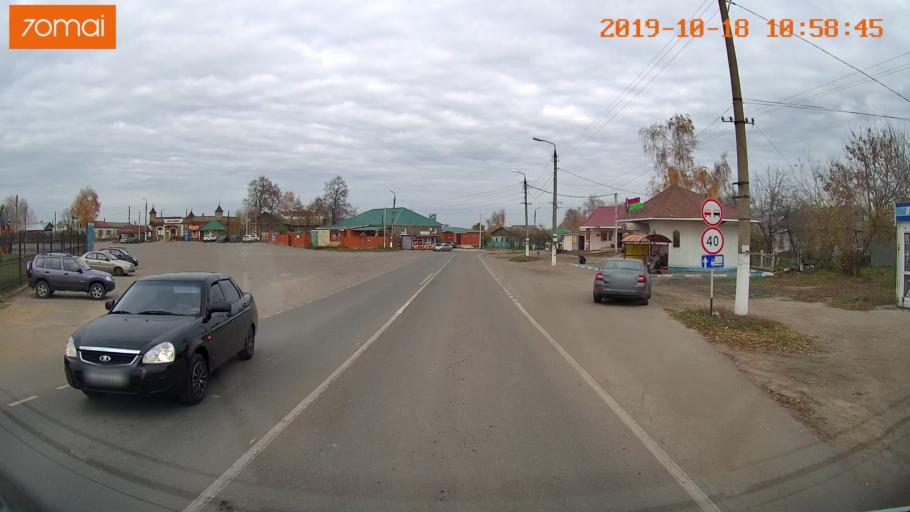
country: RU
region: Tula
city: Yepifan'
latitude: 53.8258
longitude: 38.5539
